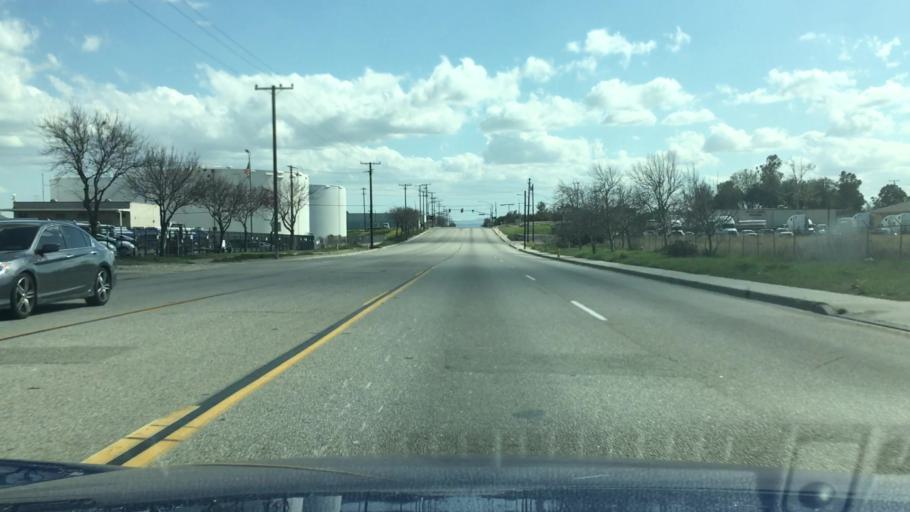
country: US
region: California
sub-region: San Bernardino County
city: Bloomington
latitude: 34.0590
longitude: -117.3703
